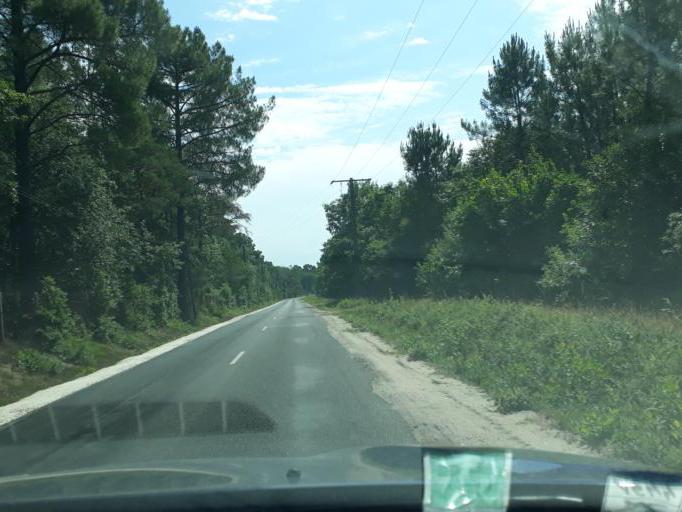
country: FR
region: Centre
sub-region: Departement du Loir-et-Cher
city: Vouzon
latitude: 47.6484
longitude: 2.0225
